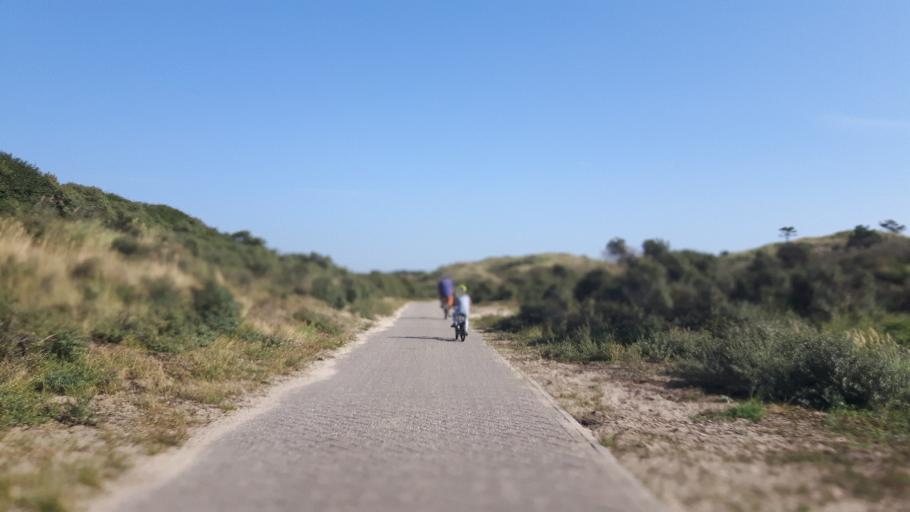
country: NL
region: North Holland
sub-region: Gemeente Zandvoort
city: Zandvoort
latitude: 52.3934
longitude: 4.5491
